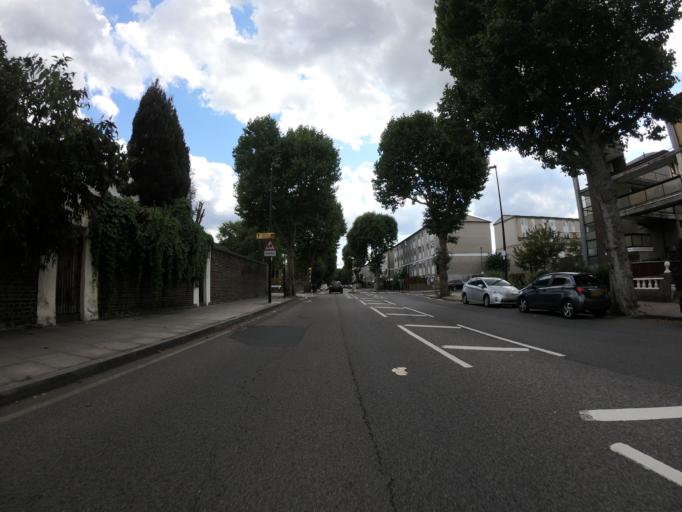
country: GB
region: England
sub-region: Greater London
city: Poplar
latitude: 51.4912
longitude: -0.0057
